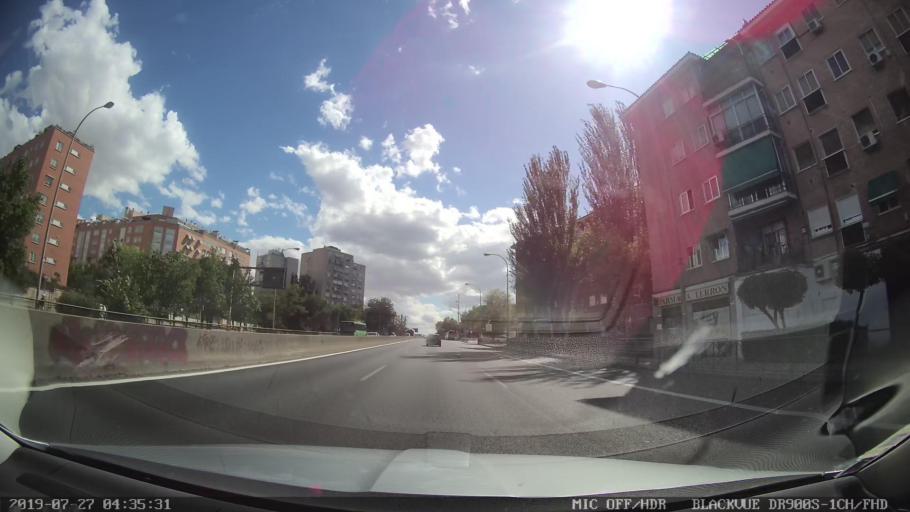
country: ES
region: Madrid
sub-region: Provincia de Madrid
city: Latina
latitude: 40.3974
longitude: -3.7671
